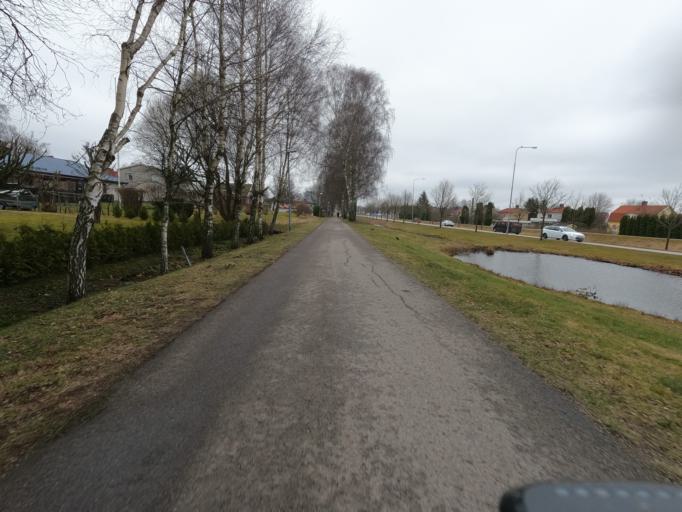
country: SE
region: Kronoberg
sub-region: Ljungby Kommun
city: Ljungby
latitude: 56.8306
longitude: 13.9249
